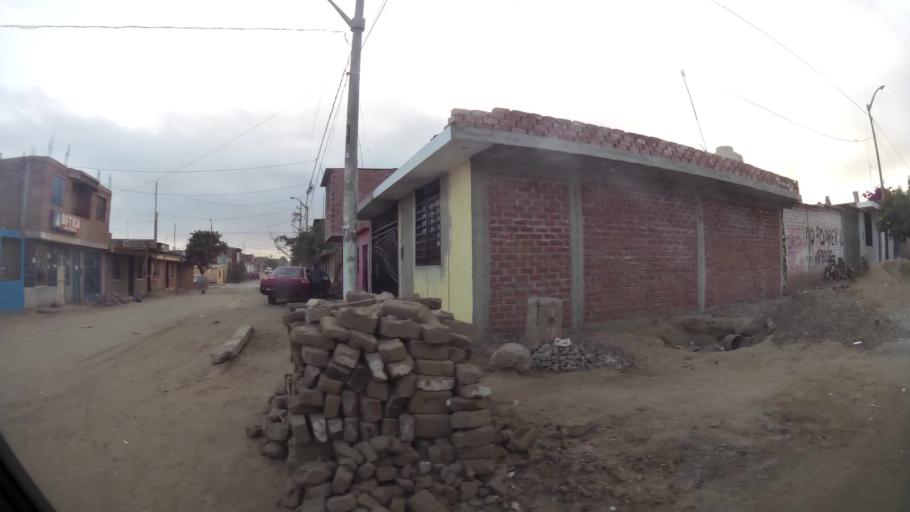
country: PE
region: La Libertad
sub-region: Provincia de Trujillo
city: El Porvenir
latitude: -8.0649
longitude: -79.0086
